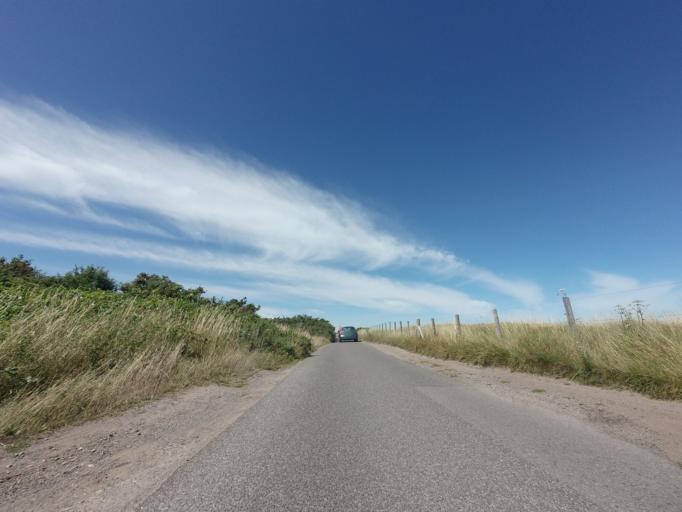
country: GB
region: England
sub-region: Kent
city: Deal
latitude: 51.2572
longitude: 1.3867
